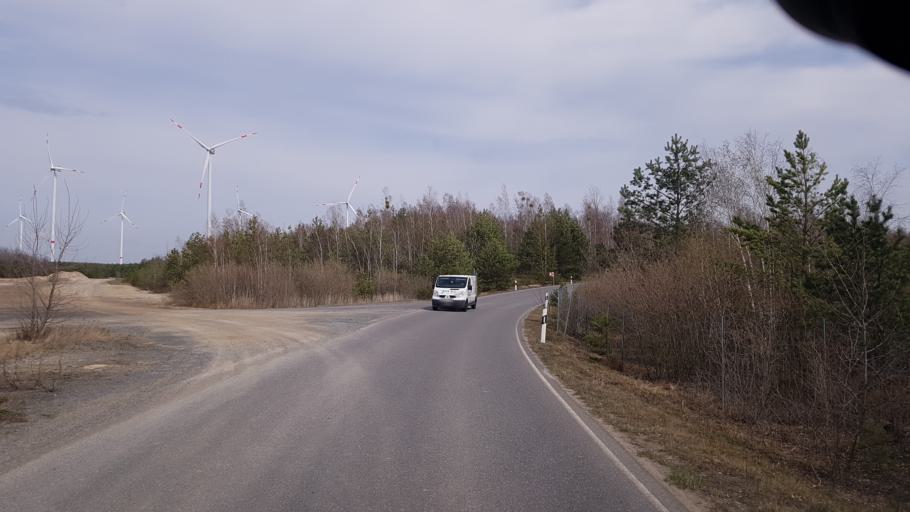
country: DE
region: Brandenburg
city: Schipkau
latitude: 51.5330
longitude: 13.8602
